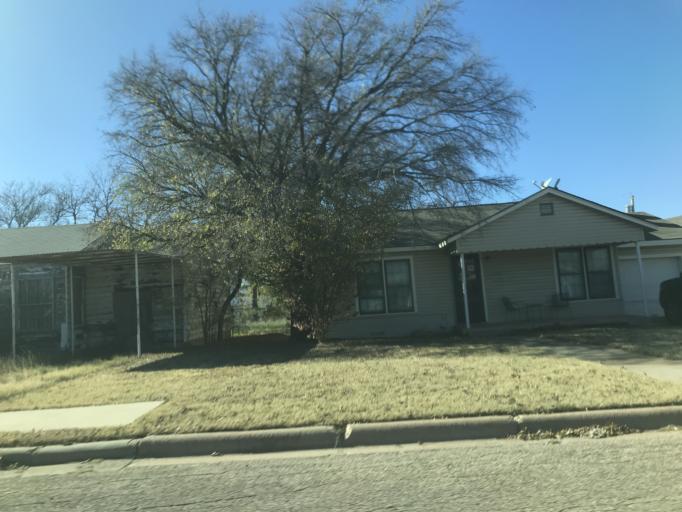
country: US
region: Texas
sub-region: Taylor County
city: Abilene
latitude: 32.4327
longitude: -99.7560
